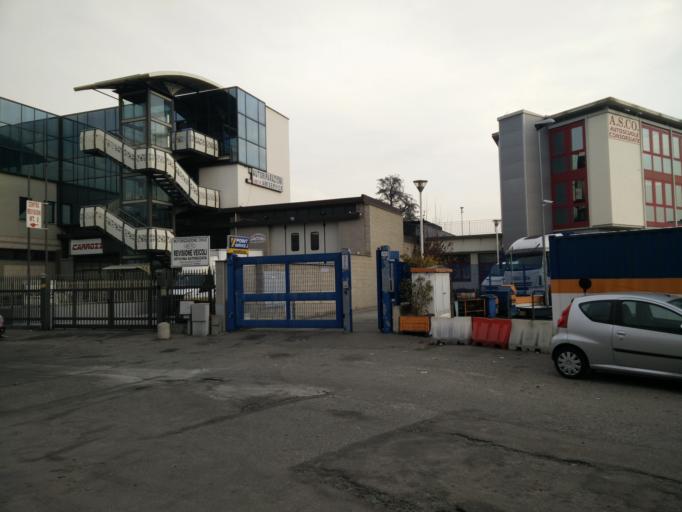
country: IT
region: Piedmont
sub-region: Provincia di Torino
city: Gerbido
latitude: 45.0328
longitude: 7.6173
